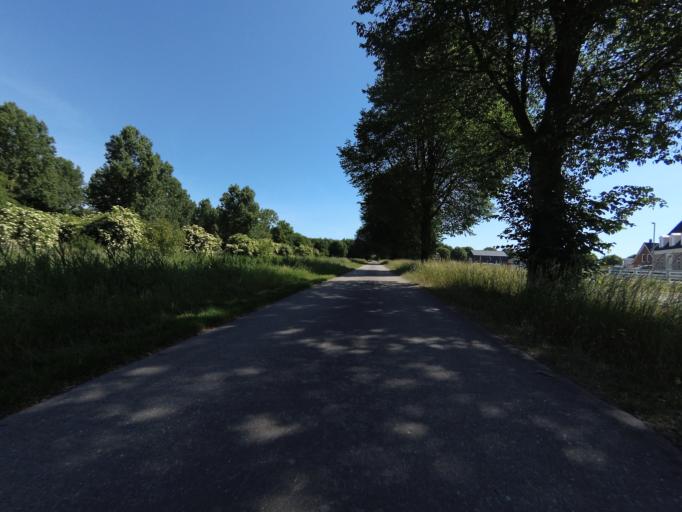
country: NL
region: Utrecht
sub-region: Gemeente Bunschoten
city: Spakenburg
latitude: 52.3292
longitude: 5.3270
